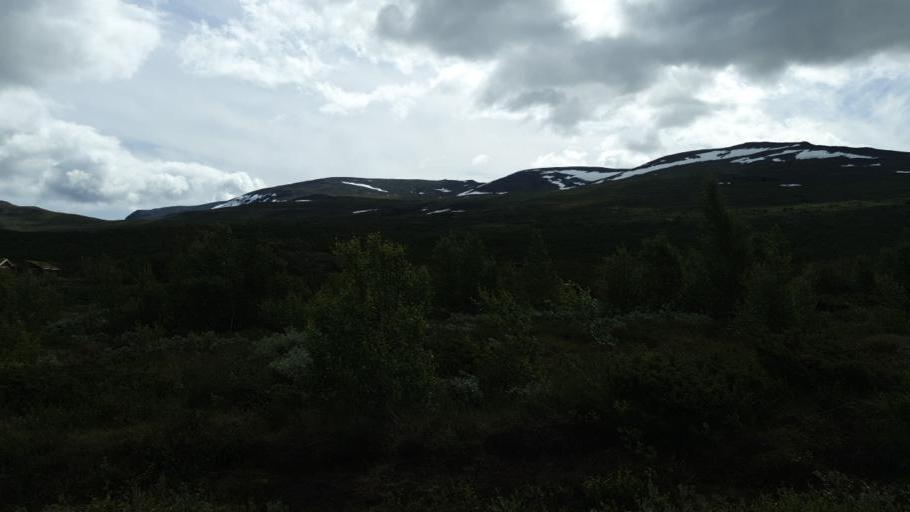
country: NO
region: Oppland
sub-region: Oystre Slidre
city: Heggenes
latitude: 61.4873
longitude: 8.8345
